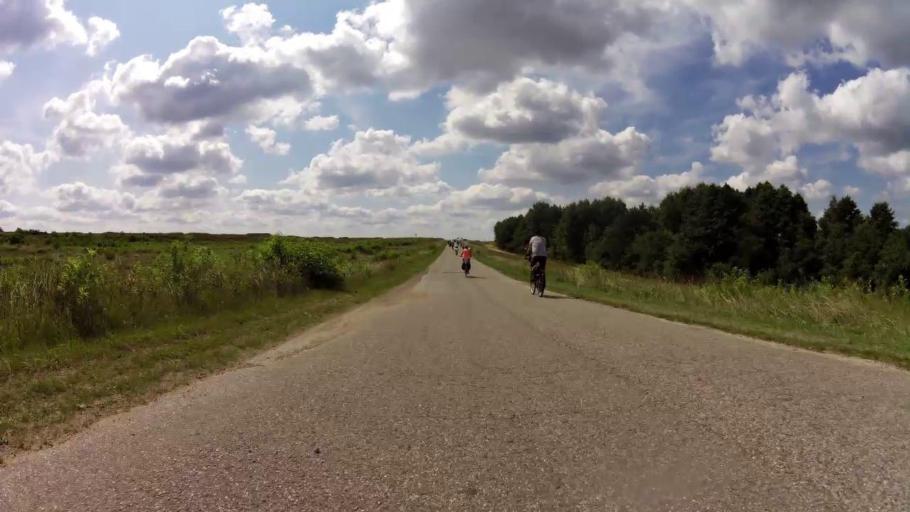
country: PL
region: West Pomeranian Voivodeship
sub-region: Powiat drawski
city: Drawsko Pomorskie
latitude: 53.4464
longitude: 15.7627
